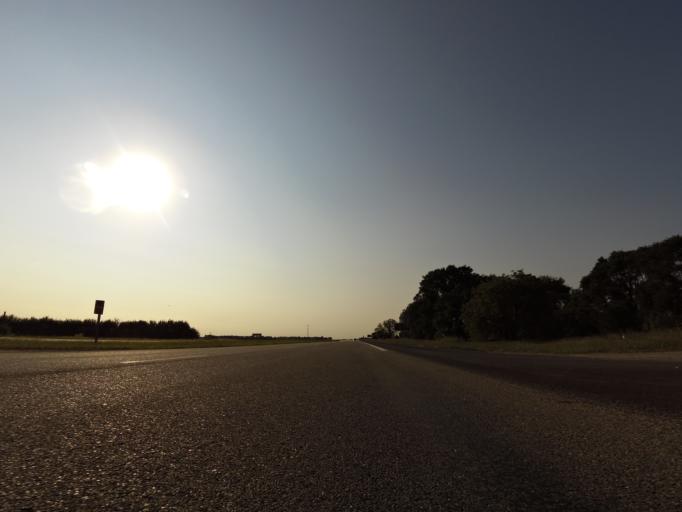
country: US
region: Kansas
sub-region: Reno County
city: Haven
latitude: 37.9293
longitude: -97.8485
